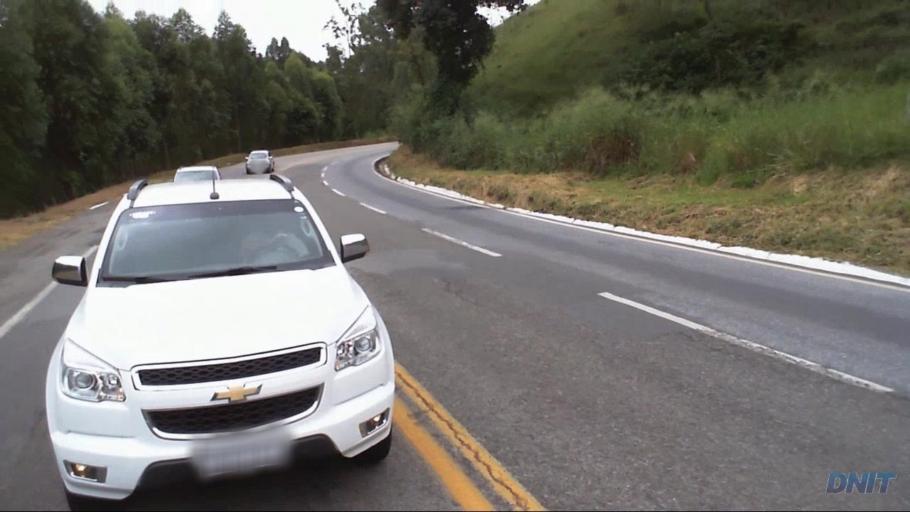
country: BR
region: Minas Gerais
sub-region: Joao Monlevade
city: Joao Monlevade
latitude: -19.8526
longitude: -43.2179
